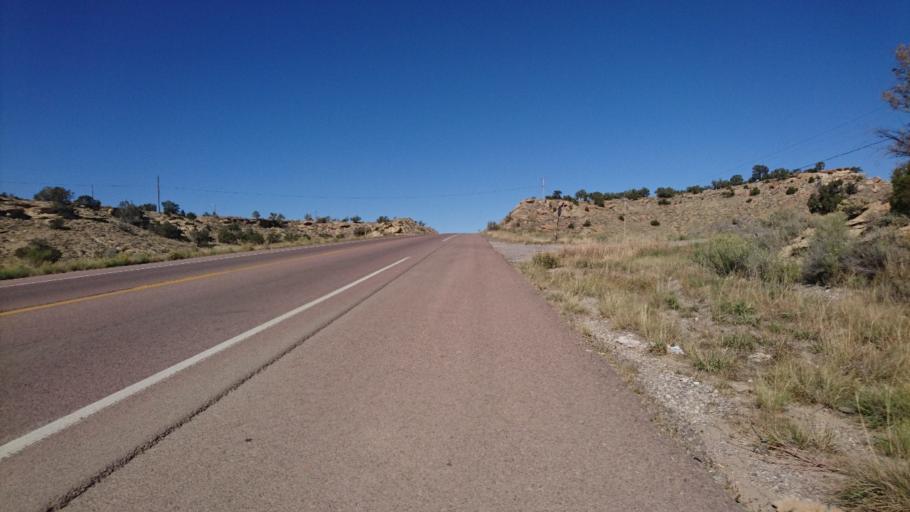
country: US
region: New Mexico
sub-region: McKinley County
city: Gallup
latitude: 35.4753
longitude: -108.7422
